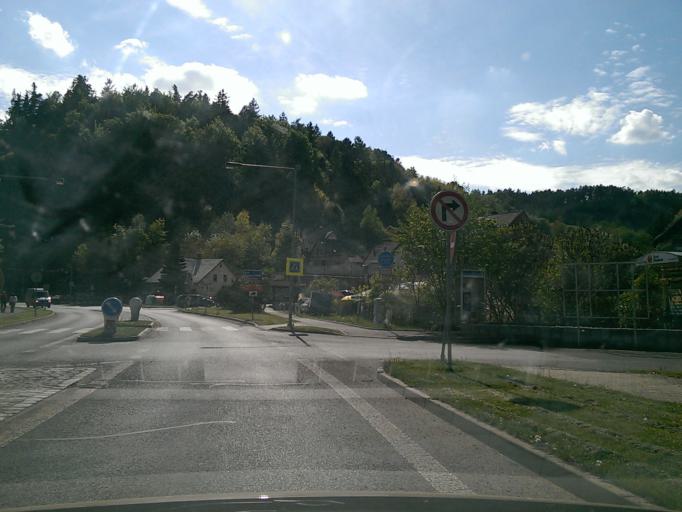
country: CZ
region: Liberecky
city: Mala Skala
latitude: 50.6431
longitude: 15.1945
